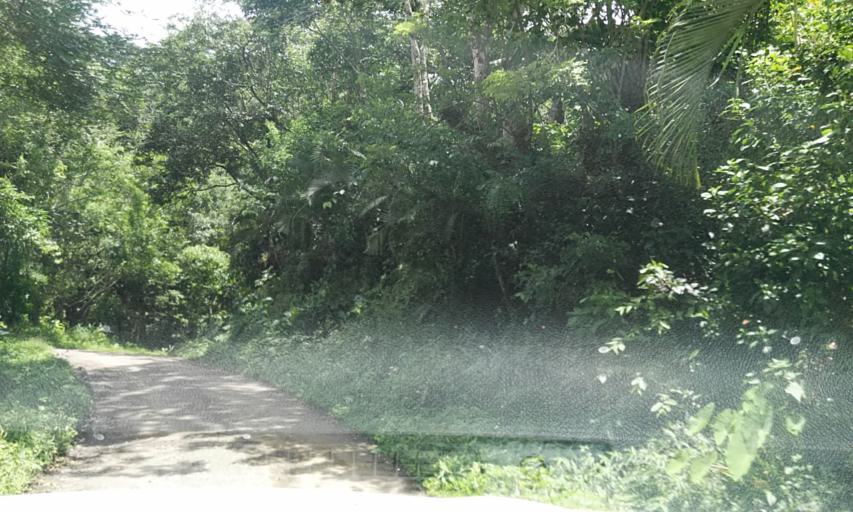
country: NI
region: Matagalpa
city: San Ramon
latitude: 12.9915
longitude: -85.8599
